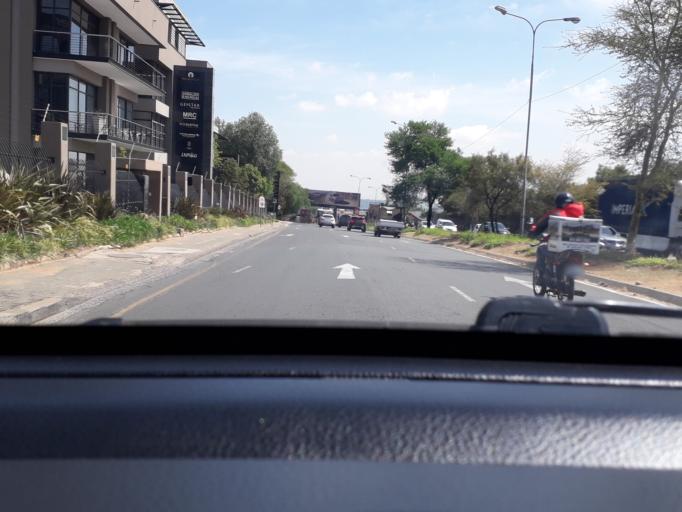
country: ZA
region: Gauteng
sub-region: City of Johannesburg Metropolitan Municipality
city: Johannesburg
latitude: -26.1195
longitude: 28.0467
